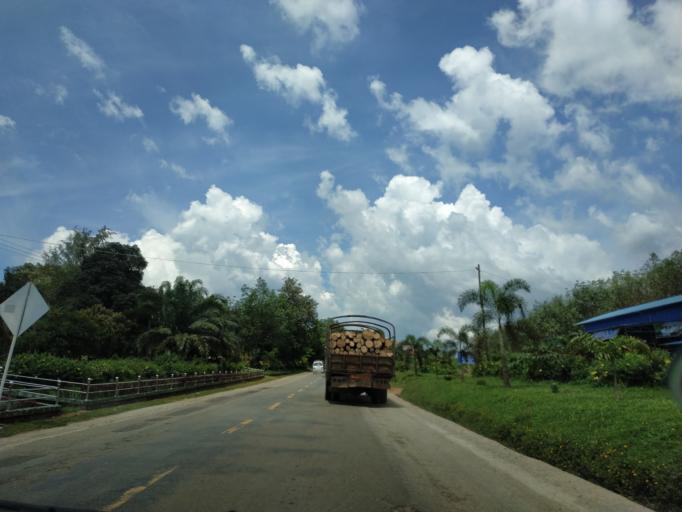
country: TH
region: Kanchanaburi
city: Sangkhla Buri
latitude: 15.2678
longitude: 97.8563
